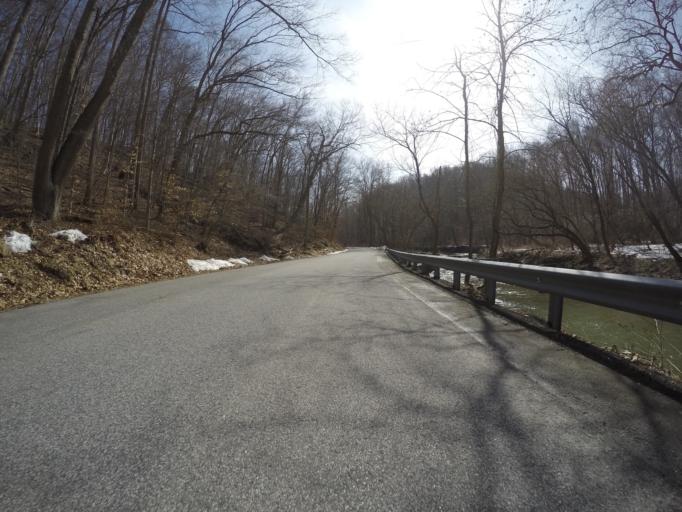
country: US
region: Maryland
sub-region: Baltimore County
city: Hunt Valley
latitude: 39.5123
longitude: -76.6598
